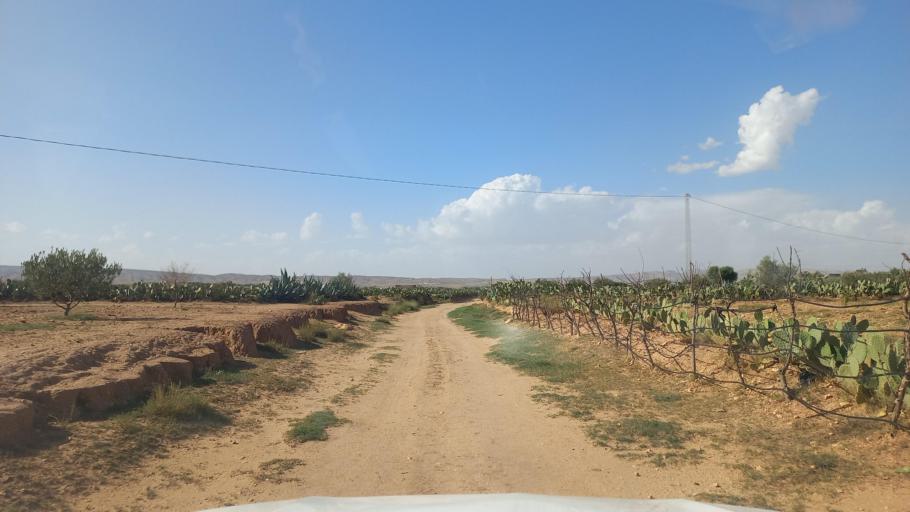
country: TN
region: Al Qasrayn
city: Sbiba
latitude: 35.3124
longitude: 9.0317
